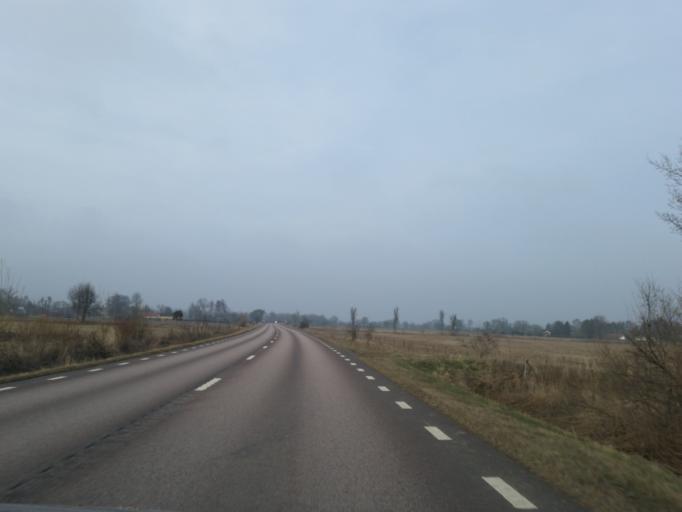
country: SE
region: Kalmar
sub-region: Borgholms Kommun
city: Borgholm
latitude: 57.1254
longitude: 16.9693
